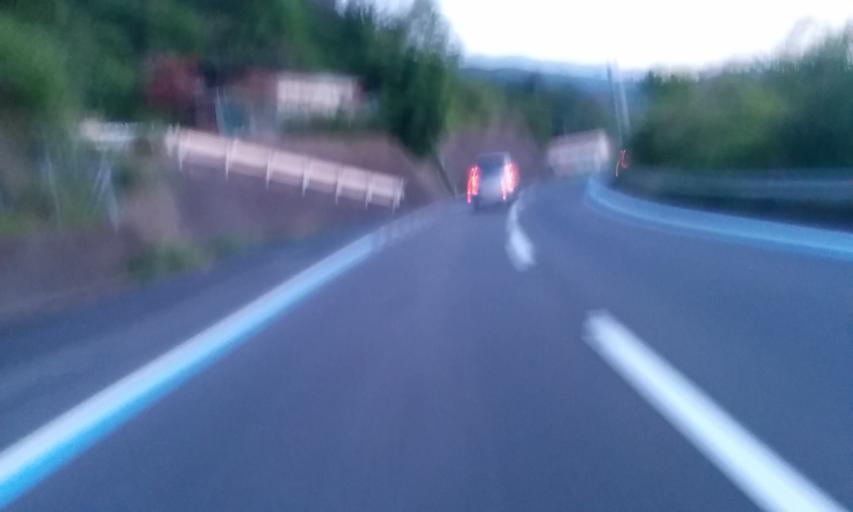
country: JP
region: Ehime
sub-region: Nishiuwa-gun
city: Ikata-cho
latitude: 33.5523
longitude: 132.4266
